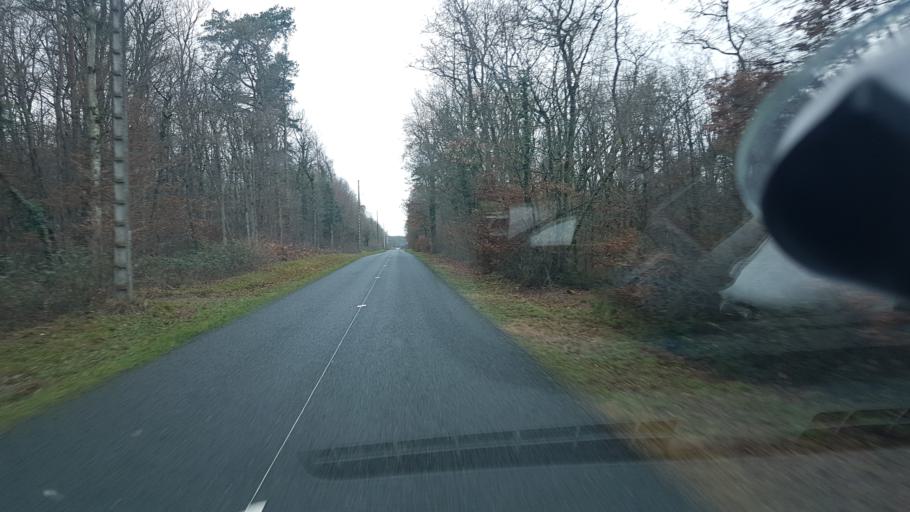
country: FR
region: Ile-de-France
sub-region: Departement de Seine-et-Marne
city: Montigny-sur-Loing
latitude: 48.2757
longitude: 2.7730
